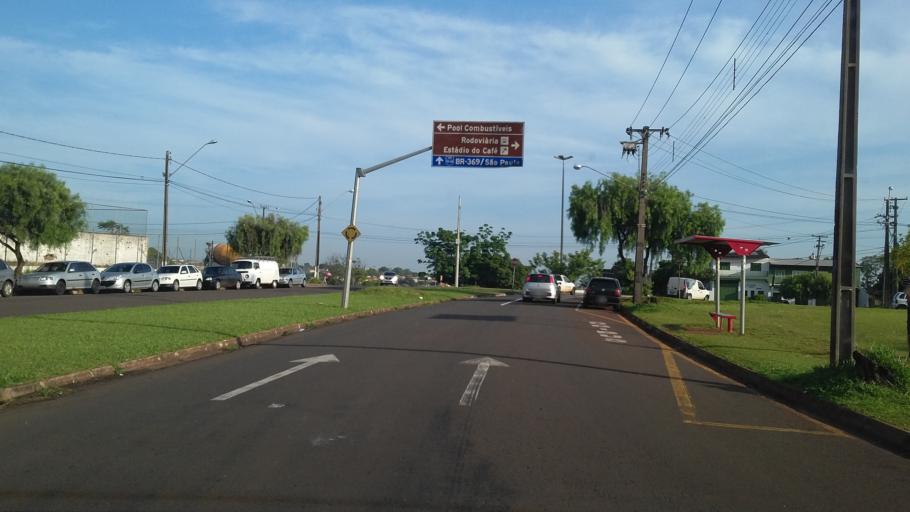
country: BR
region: Parana
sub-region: Londrina
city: Londrina
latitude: -23.2979
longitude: -51.1903
